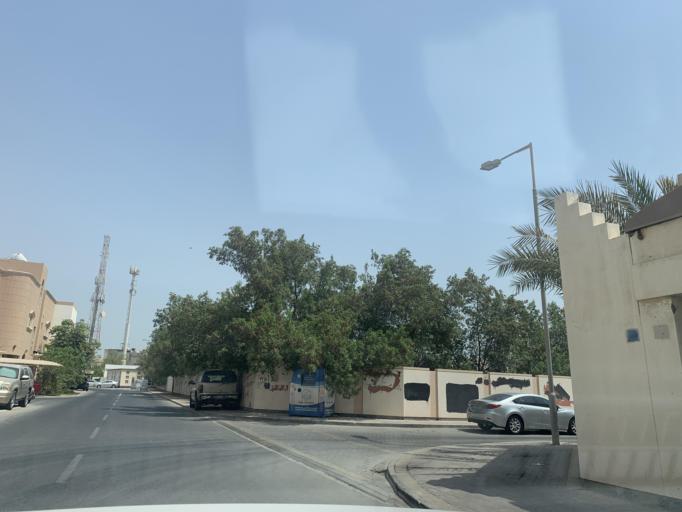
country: BH
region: Manama
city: Jidd Hafs
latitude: 26.2098
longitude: 50.5060
